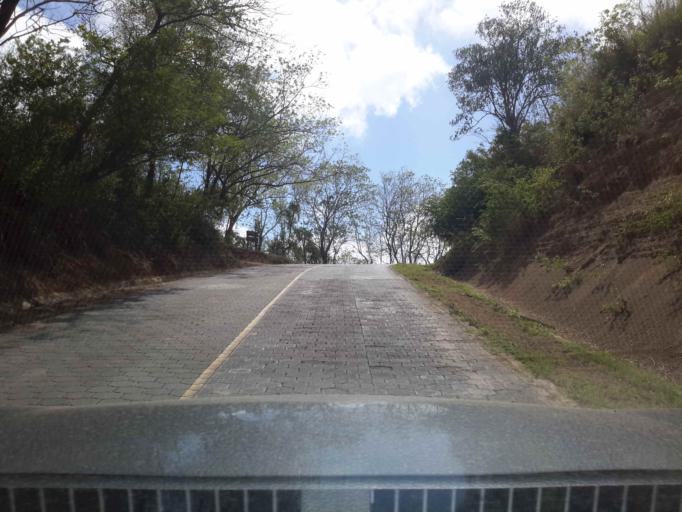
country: NI
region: Rivas
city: San Juan del Sur
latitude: 11.2229
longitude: -85.8165
